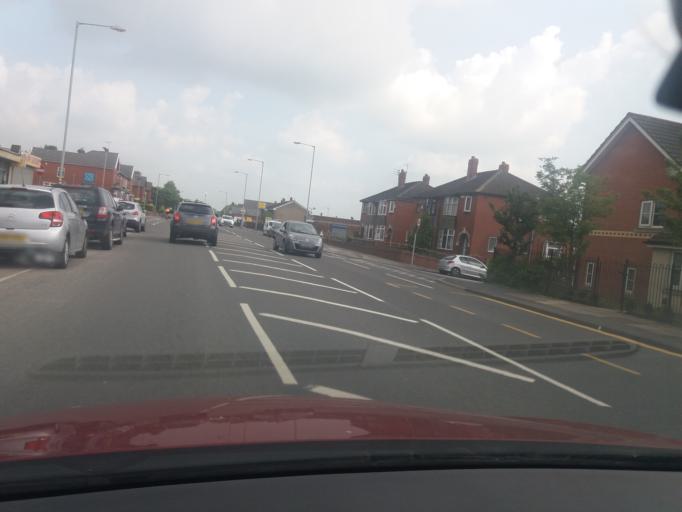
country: GB
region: England
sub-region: Borough of Bolton
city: Horwich
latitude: 53.5895
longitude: -2.5342
